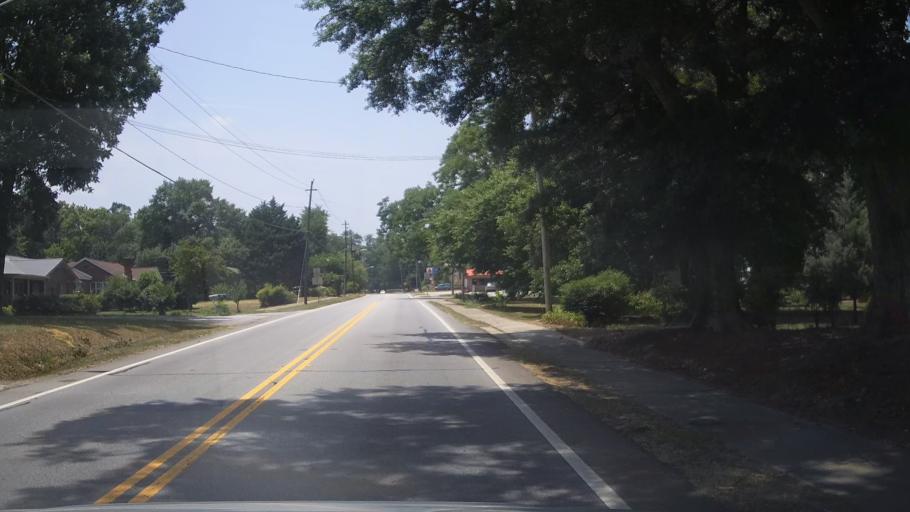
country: US
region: Georgia
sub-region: Hart County
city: Royston
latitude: 34.2881
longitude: -83.1017
